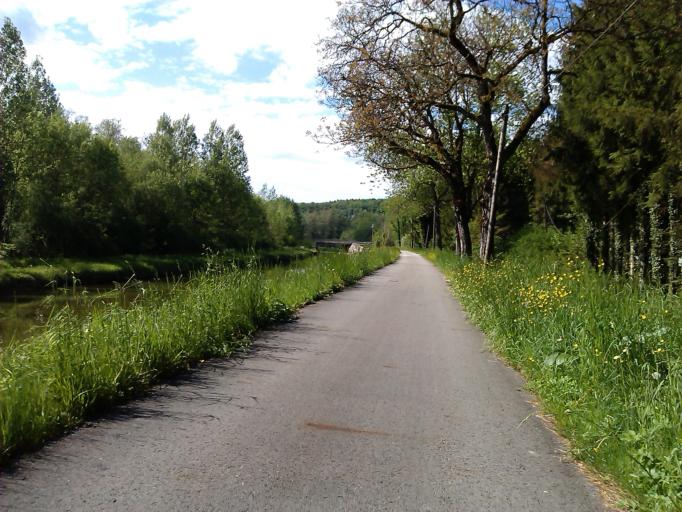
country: FR
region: Franche-Comte
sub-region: Departement du Doubs
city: Montenois
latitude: 47.4489
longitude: 6.5963
